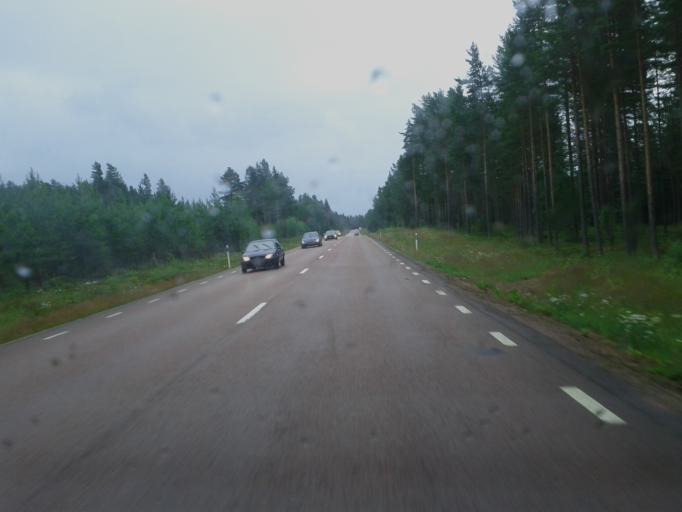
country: SE
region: Dalarna
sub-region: Mora Kommun
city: Mora
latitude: 60.9594
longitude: 14.7188
